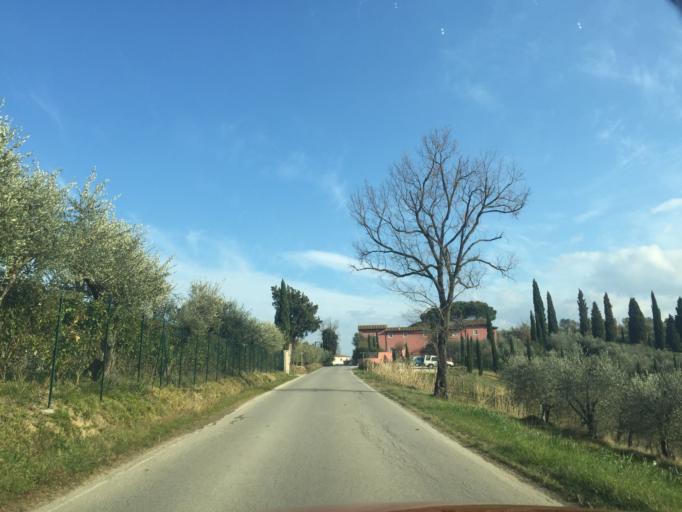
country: IT
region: Tuscany
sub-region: Province of Florence
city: Stabbia
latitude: 43.7639
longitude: 10.8441
